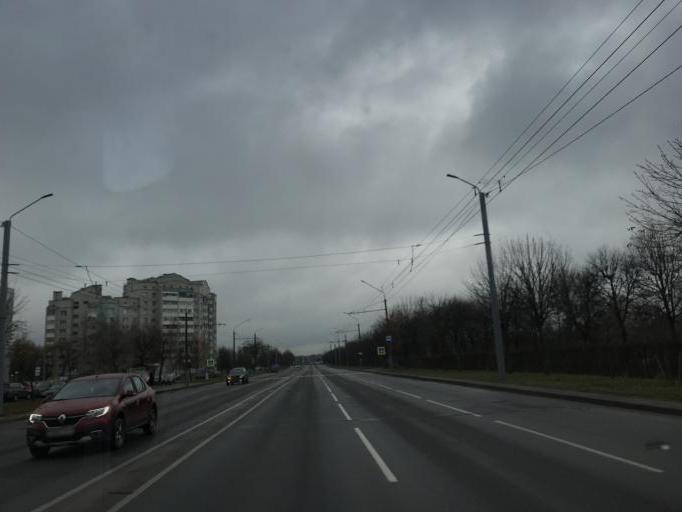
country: BY
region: Mogilev
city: Mahilyow
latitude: 53.8664
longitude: 30.3301
